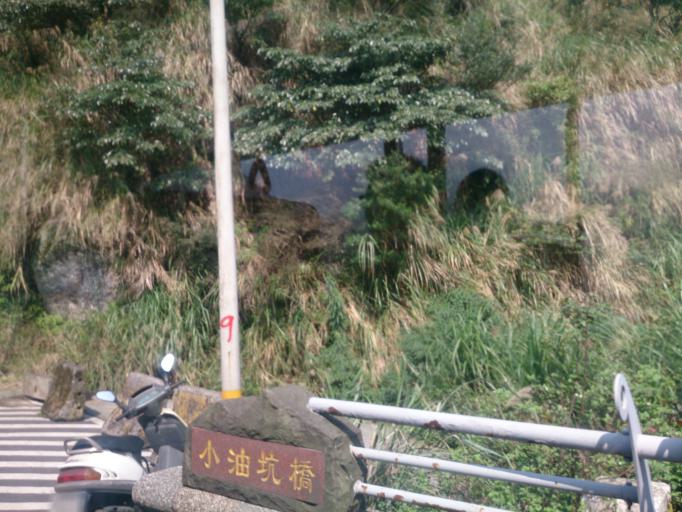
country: TW
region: Taipei
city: Taipei
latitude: 25.1766
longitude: 121.5444
